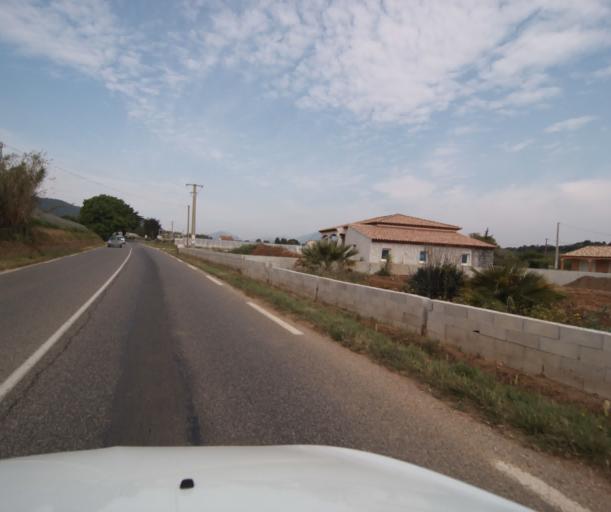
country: FR
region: Provence-Alpes-Cote d'Azur
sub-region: Departement du Var
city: Hyeres
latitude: 43.1132
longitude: 6.1040
